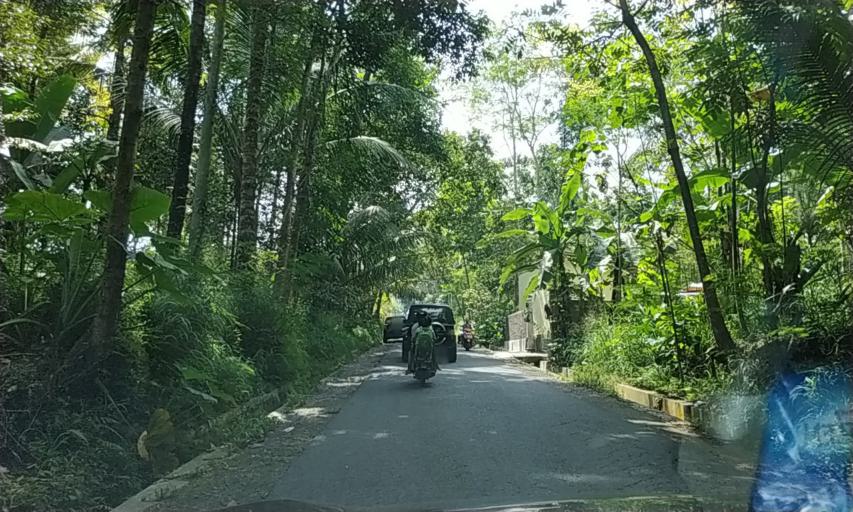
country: ID
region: Central Java
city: Jogonalan
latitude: -7.6328
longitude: 110.4685
